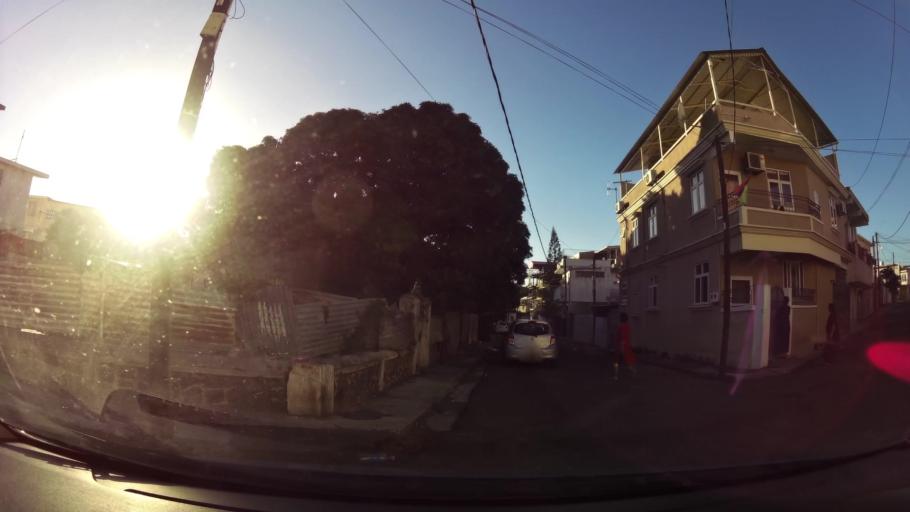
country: MU
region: Port Louis
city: Port Louis
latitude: -20.1729
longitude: 57.5086
